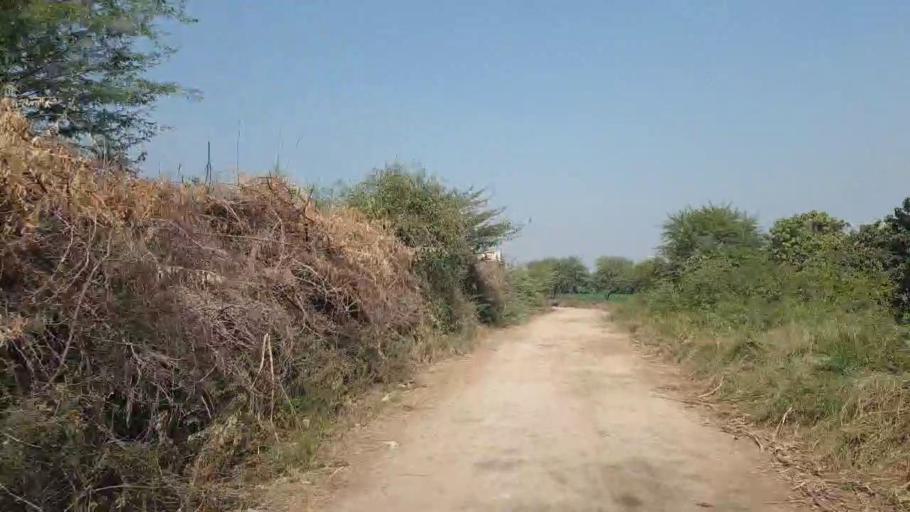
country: PK
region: Sindh
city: Chambar
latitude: 25.4051
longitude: 68.9018
